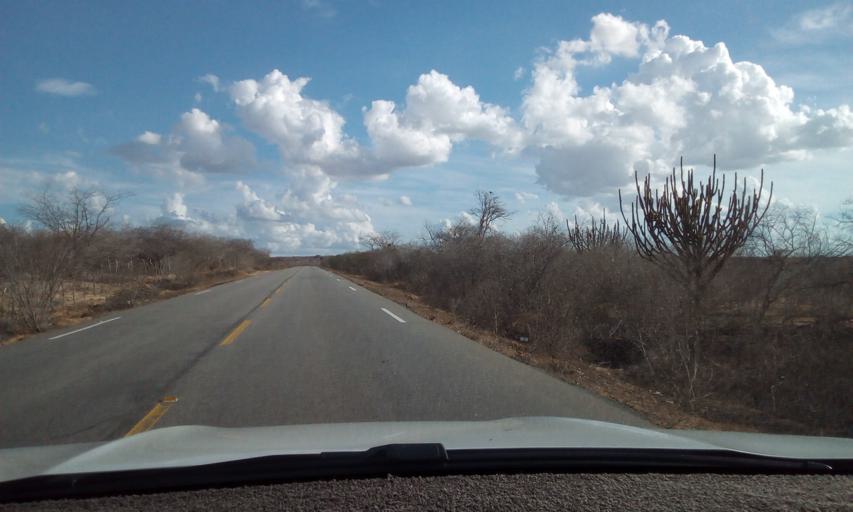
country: BR
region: Paraiba
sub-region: Soledade
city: Soledade
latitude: -6.8724
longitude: -36.4006
